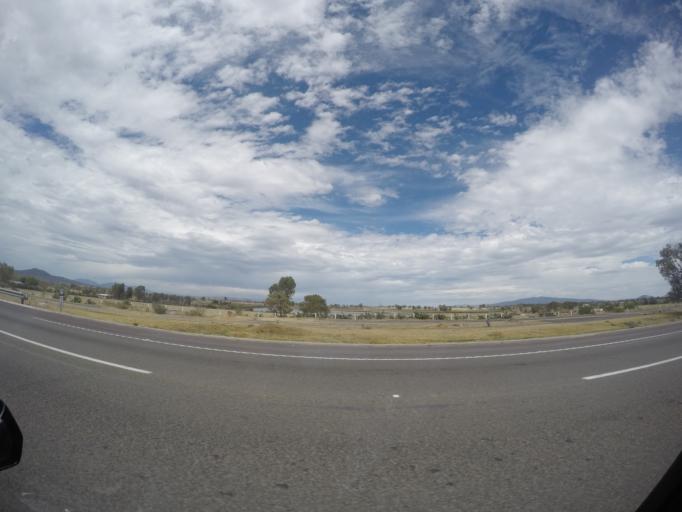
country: MX
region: Hidalgo
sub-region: Huichapan
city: Llano Largo
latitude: 20.2325
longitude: -99.8187
